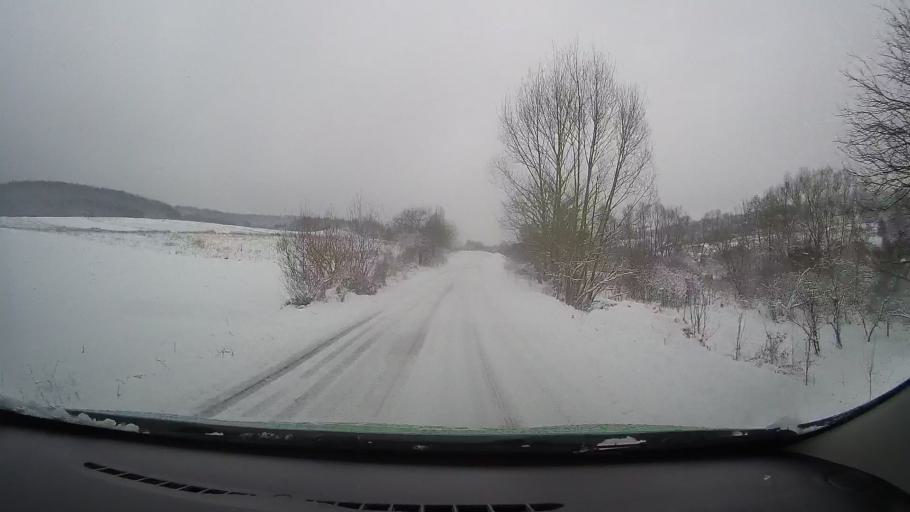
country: RO
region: Hunedoara
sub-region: Comuna Carjiti
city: Carjiti
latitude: 45.8250
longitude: 22.8570
